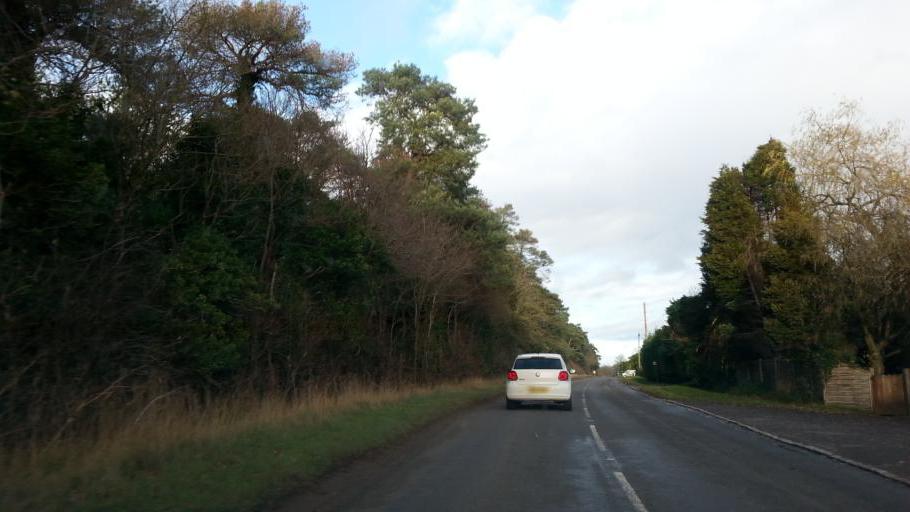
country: GB
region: England
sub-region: Oxfordshire
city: Stanford in the Vale
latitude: 51.6573
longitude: -1.4991
